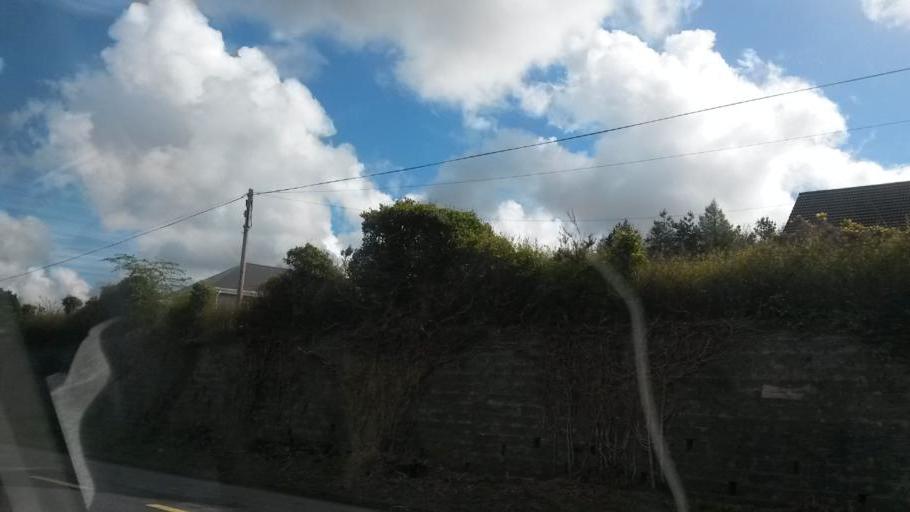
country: IE
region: Ulster
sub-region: An Cabhan
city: Ballyjamesduff
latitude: 53.9306
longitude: -7.2171
